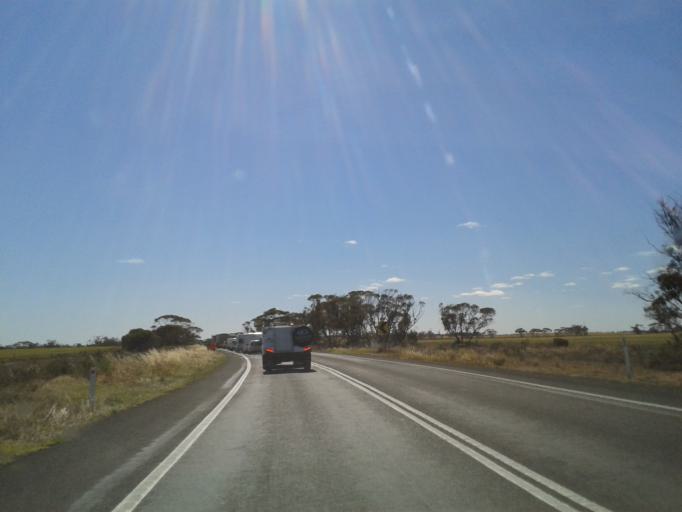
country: AU
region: New South Wales
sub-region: Wentworth
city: Dareton
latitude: -34.2760
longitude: 141.7900
